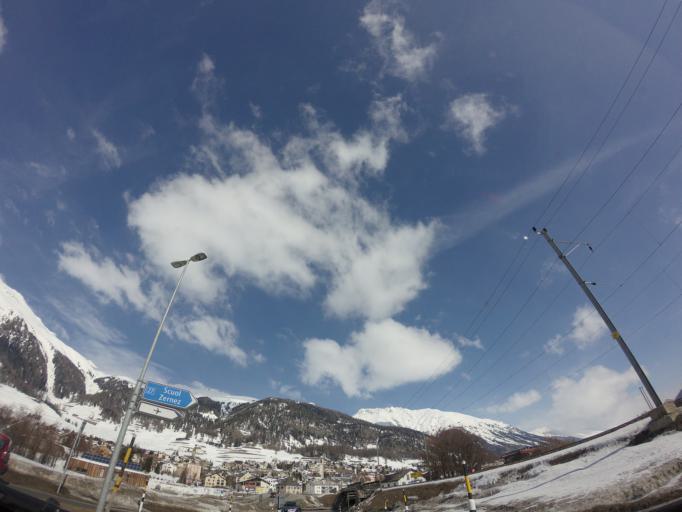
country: CH
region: Grisons
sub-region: Maloja District
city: Samedan
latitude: 46.5296
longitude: 9.8719
